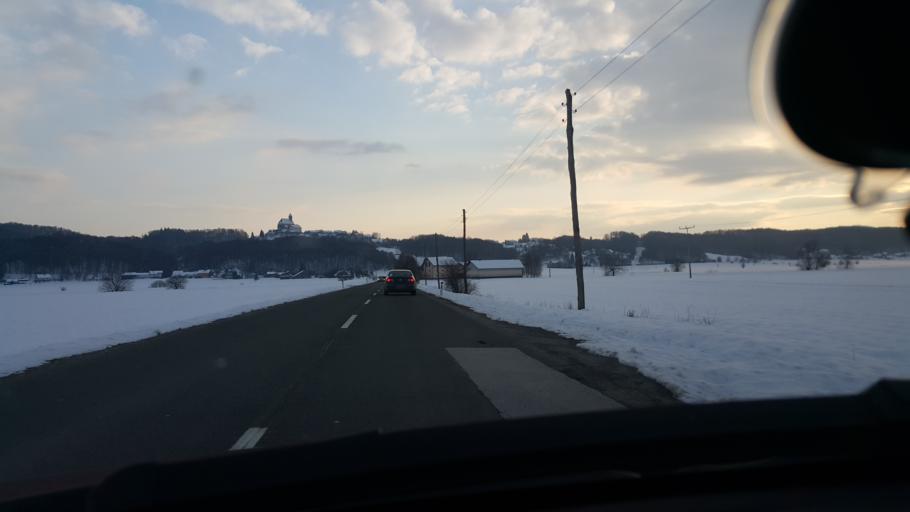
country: SI
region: Majsperk
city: Majsperk
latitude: 46.3691
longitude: 15.7667
